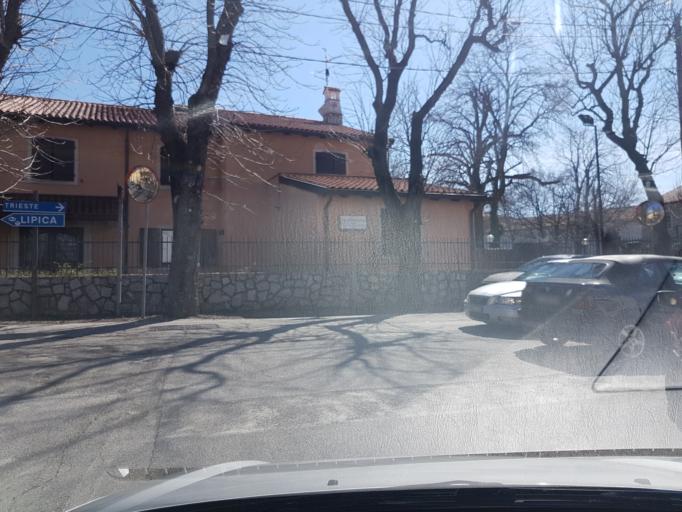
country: IT
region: Friuli Venezia Giulia
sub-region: Provincia di Trieste
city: Dolina
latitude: 45.6417
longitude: 13.8634
